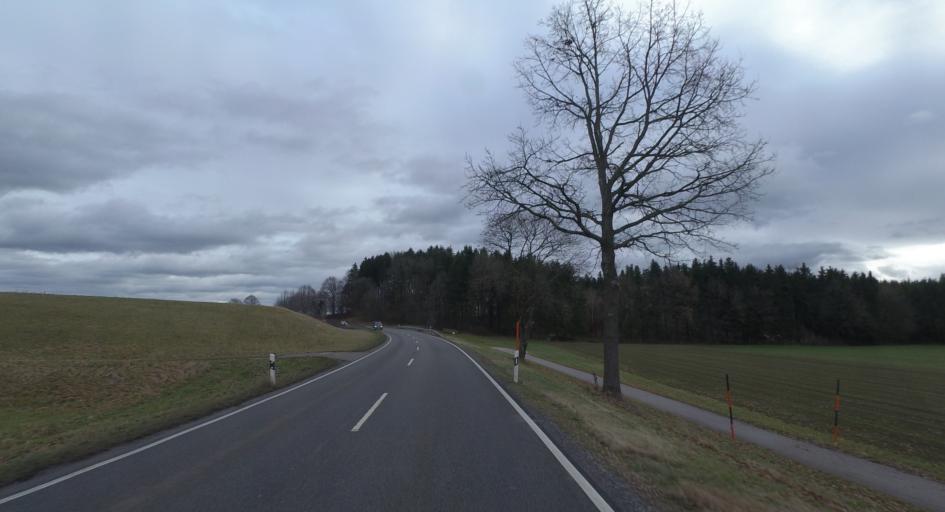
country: DE
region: Bavaria
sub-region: Upper Bavaria
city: Vachendorf
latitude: 47.8718
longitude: 12.6033
